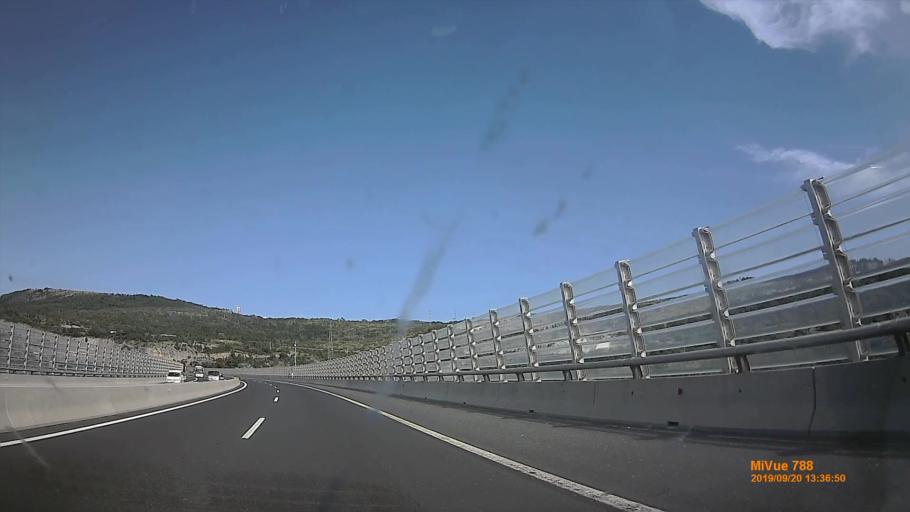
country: SI
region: Koper-Capodistria
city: Sv. Anton
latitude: 45.5538
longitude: 13.8686
